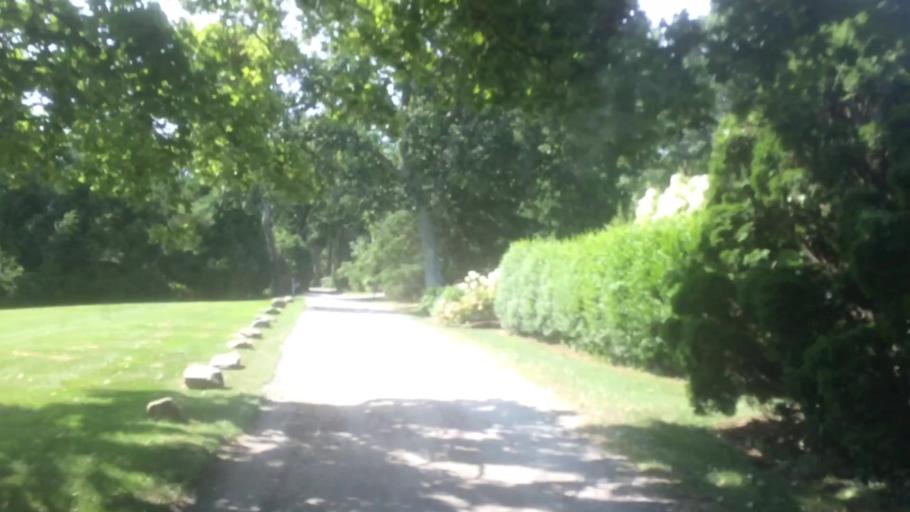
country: US
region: Rhode Island
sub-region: Newport County
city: Jamestown
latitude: 41.5052
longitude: -71.4202
